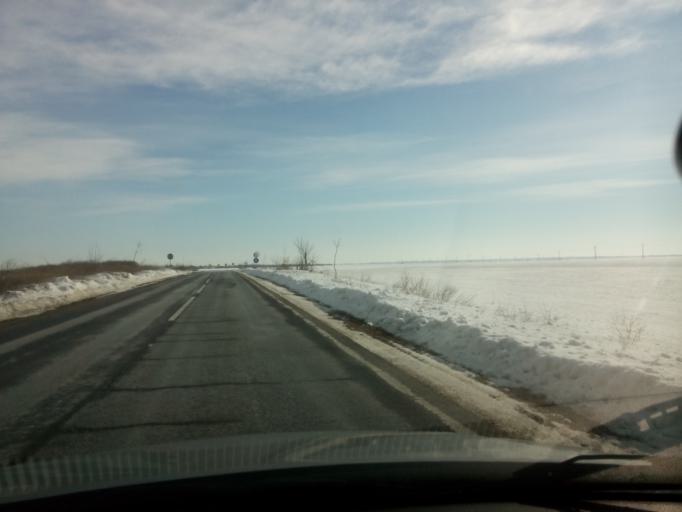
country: RO
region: Giurgiu
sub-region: Comuna Herasti
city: Herasti
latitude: 44.2420
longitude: 26.3894
